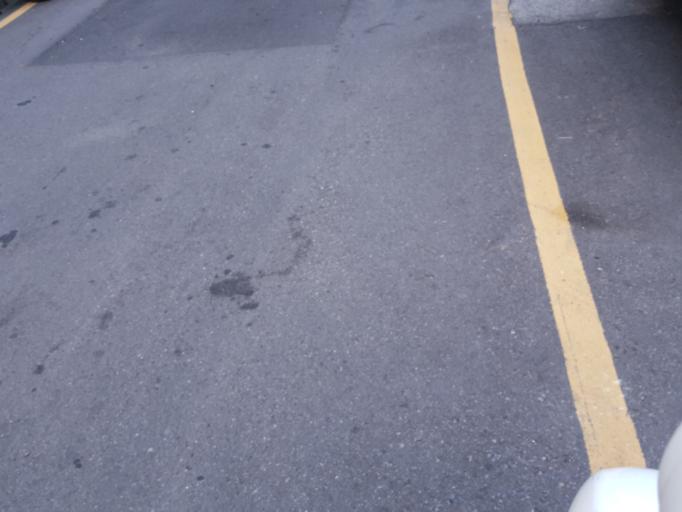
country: TW
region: Taiwan
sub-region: Hsinchu
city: Hsinchu
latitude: 24.8064
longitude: 120.9667
